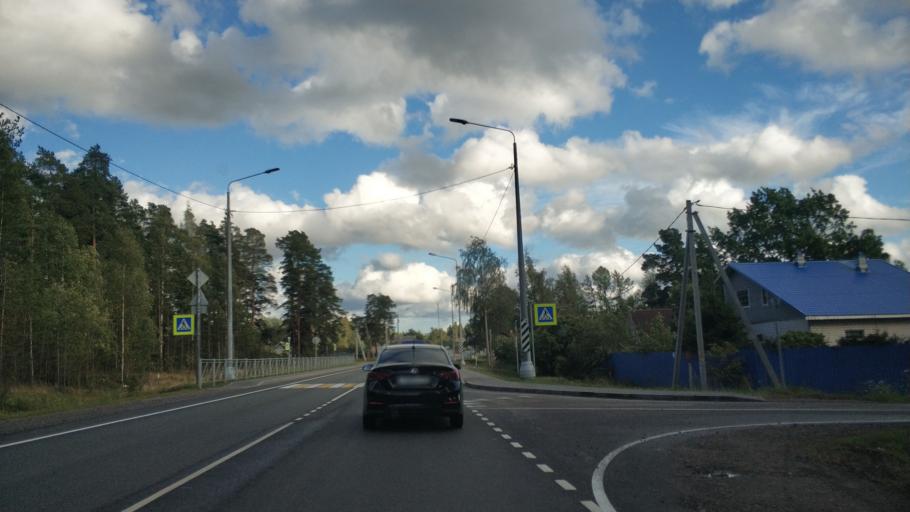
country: RU
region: Leningrad
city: Priozersk
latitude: 61.0078
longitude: 30.1743
